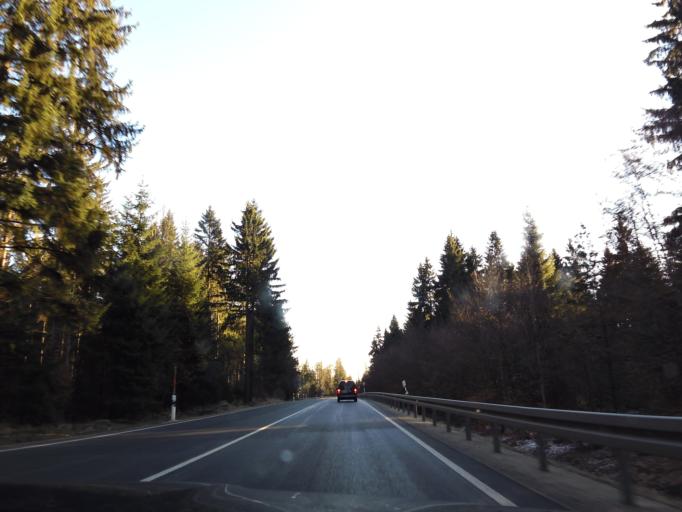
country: DE
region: Bavaria
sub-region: Upper Franconia
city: Fichtelberg
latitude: 50.0145
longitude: 11.8786
